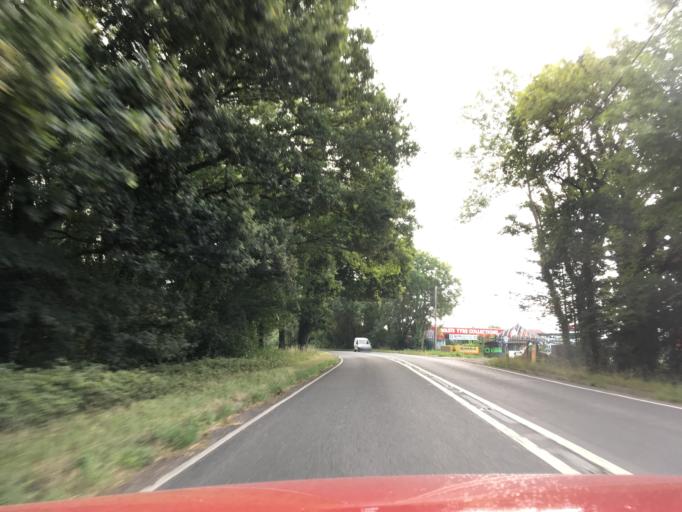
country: GB
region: England
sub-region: Hampshire
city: Colden Common
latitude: 50.9850
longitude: -1.3022
